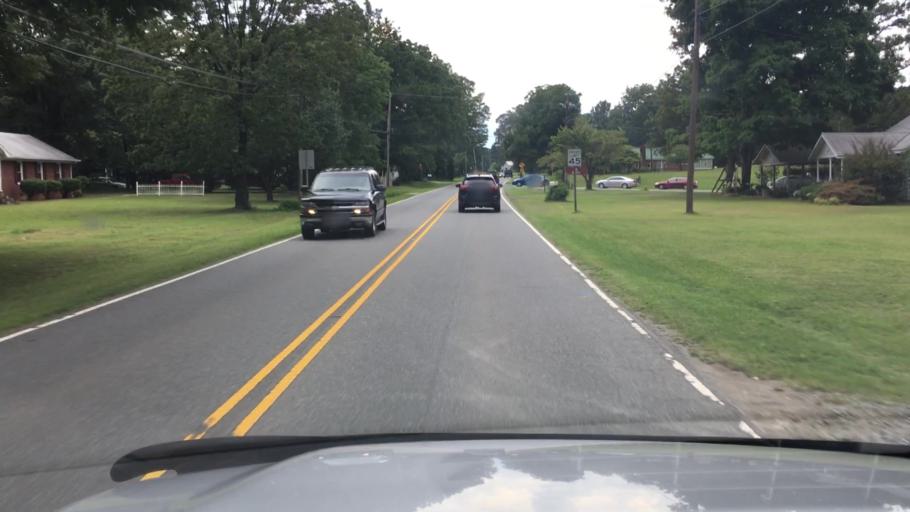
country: US
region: North Carolina
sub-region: Mecklenburg County
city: Huntersville
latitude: 35.3342
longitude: -80.8746
